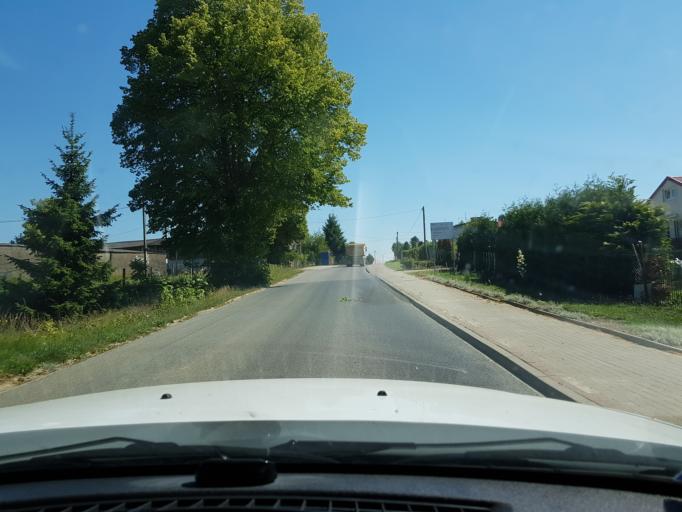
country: PL
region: West Pomeranian Voivodeship
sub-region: Powiat koszalinski
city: Mielno
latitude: 54.1980
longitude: 16.0542
